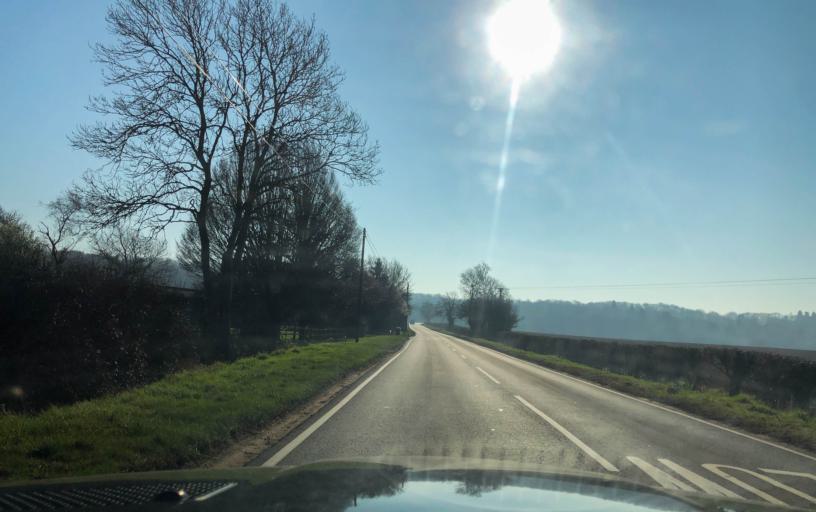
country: GB
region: England
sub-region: Warwickshire
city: Wellesbourne Mountford
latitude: 52.1851
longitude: -1.5782
